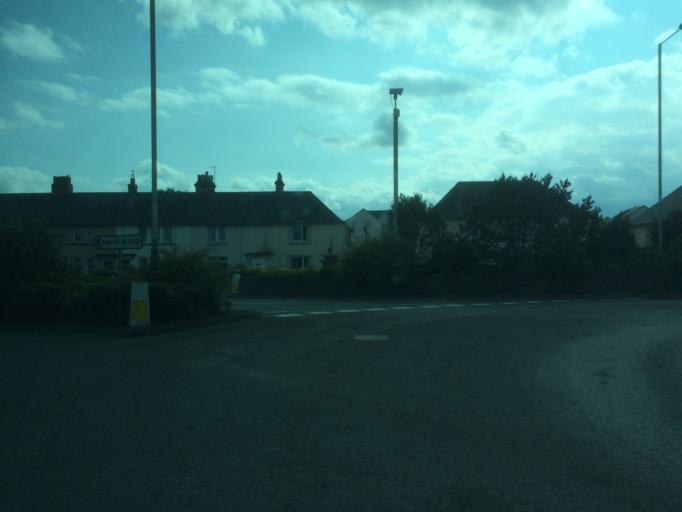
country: GB
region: Scotland
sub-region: Perth and Kinross
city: Perth
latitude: 56.4064
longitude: -3.4460
